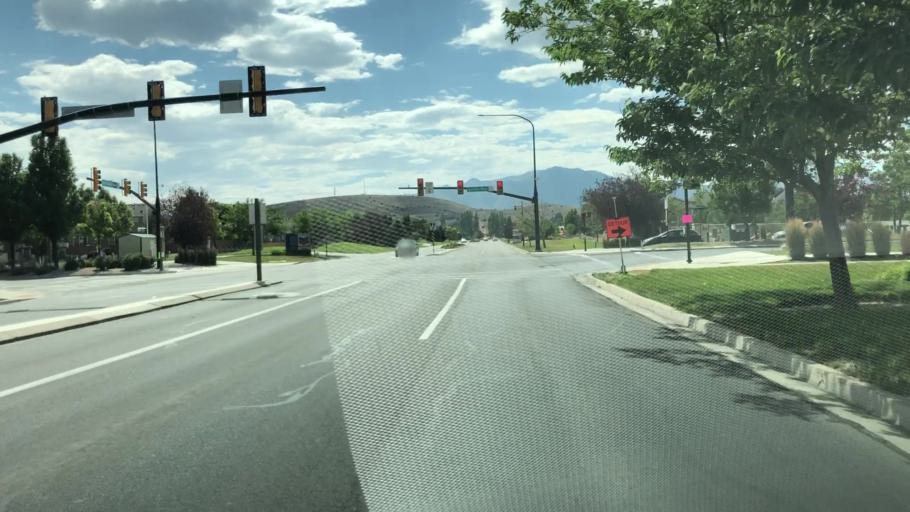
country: US
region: Utah
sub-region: Utah County
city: Eagle Mountain
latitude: 40.3623
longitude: -111.9760
